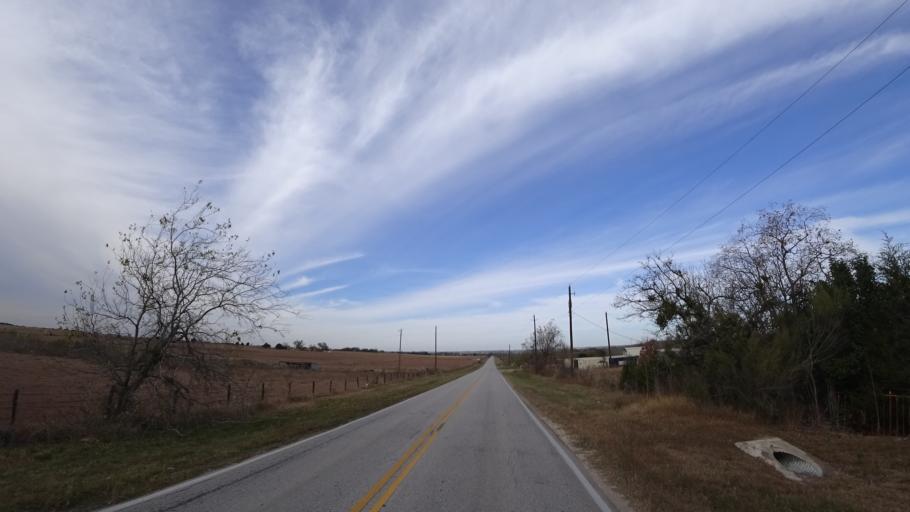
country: US
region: Texas
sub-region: Travis County
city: Onion Creek
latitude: 30.1374
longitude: -97.7196
